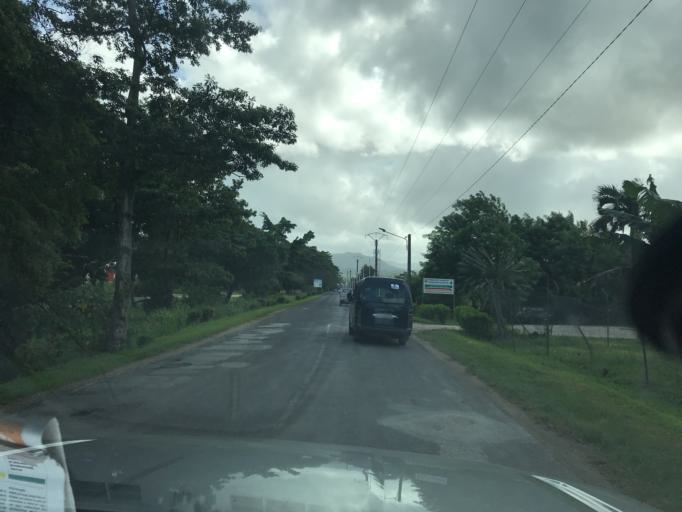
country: VU
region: Shefa
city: Port-Vila
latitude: -17.7059
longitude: 168.3175
